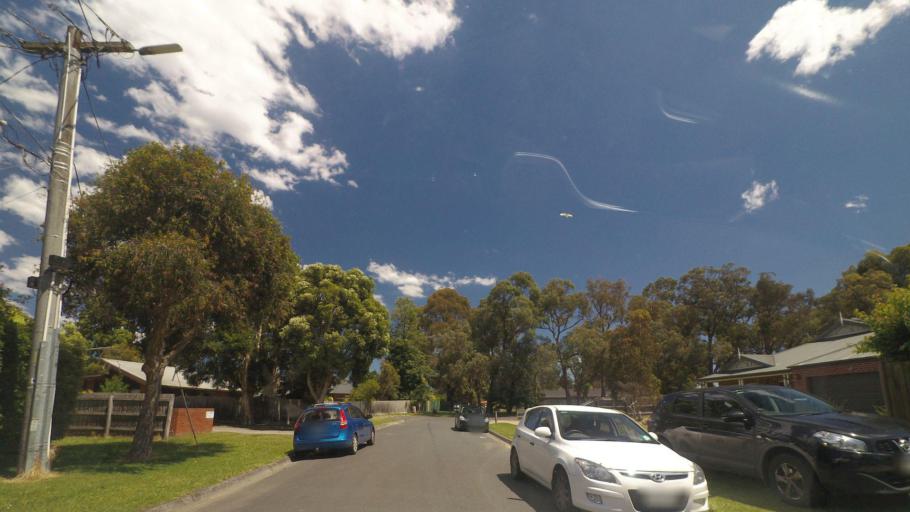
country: AU
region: Victoria
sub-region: Yarra Ranges
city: Kilsyth
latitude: -37.8079
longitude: 145.3124
